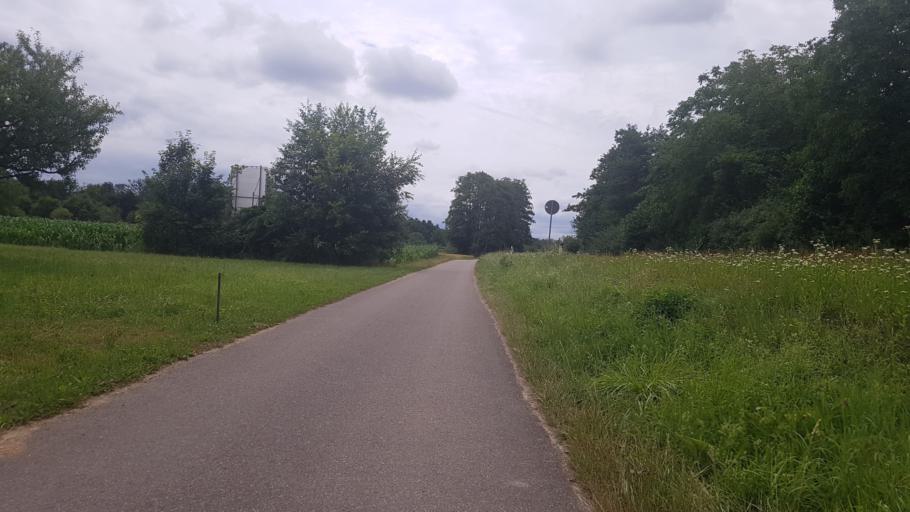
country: DE
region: Baden-Wuerttemberg
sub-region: Karlsruhe Region
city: Otigheim
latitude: 48.8904
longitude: 8.2142
